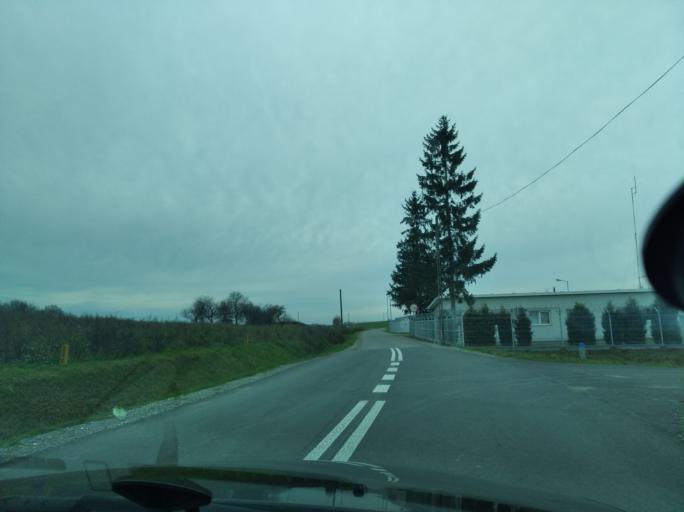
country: PL
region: Subcarpathian Voivodeship
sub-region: Powiat przeworski
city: Grzeska
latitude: 50.0651
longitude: 22.4699
